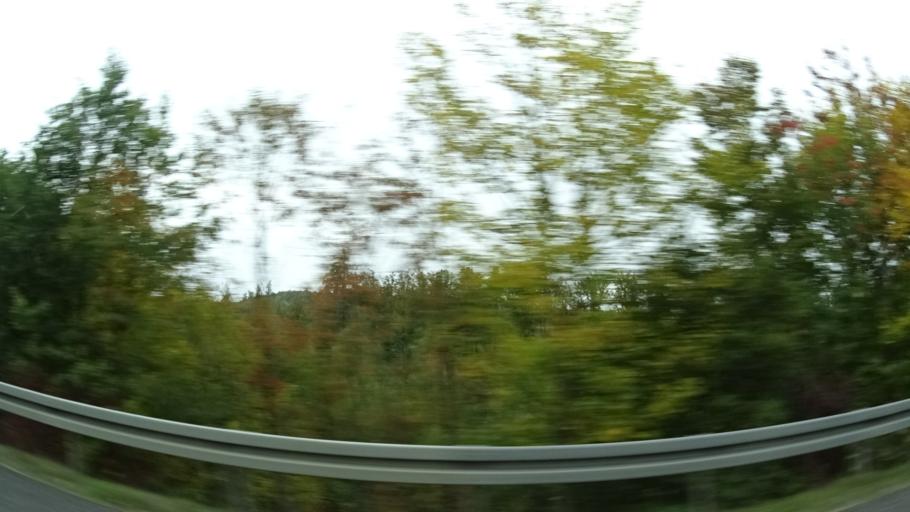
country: DE
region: Hesse
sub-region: Regierungsbezirk Darmstadt
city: Schluchtern
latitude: 50.3793
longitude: 9.5183
